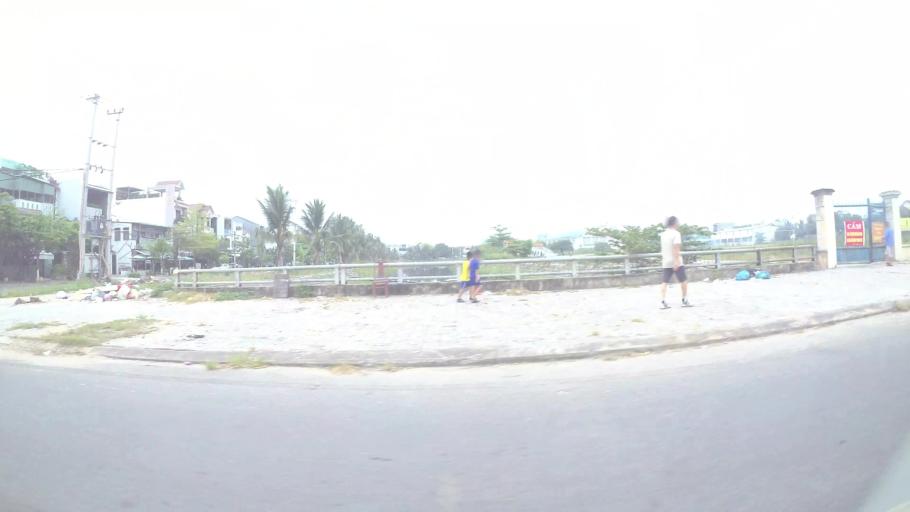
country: VN
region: Da Nang
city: Thanh Khe
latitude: 16.0599
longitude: 108.1828
